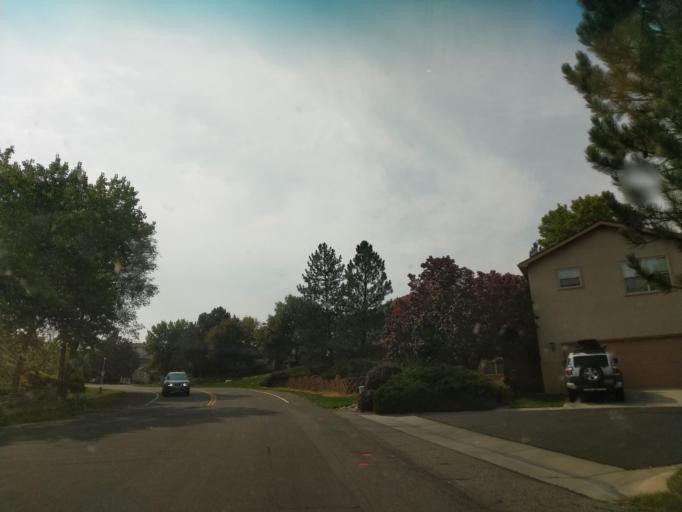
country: US
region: Colorado
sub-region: Mesa County
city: Redlands
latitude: 39.0631
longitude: -108.6100
